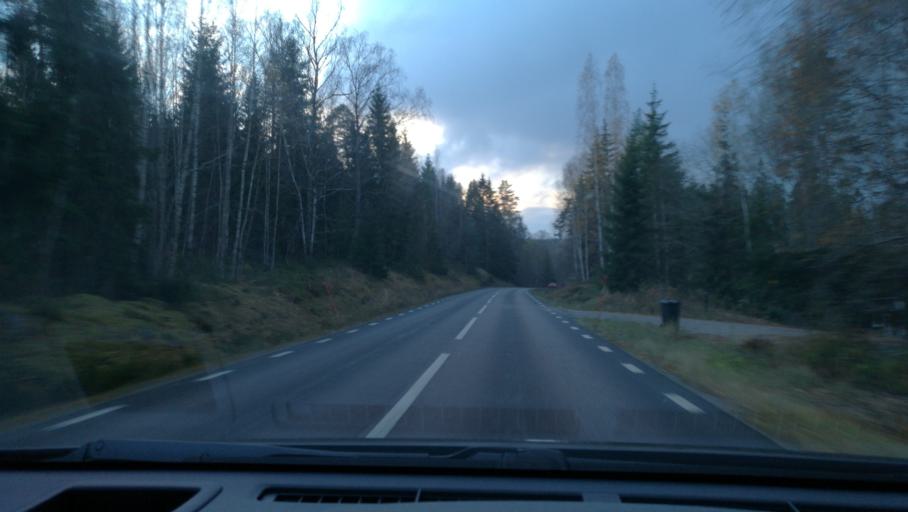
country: SE
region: Soedermanland
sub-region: Vingakers Kommun
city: Vingaker
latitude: 59.1350
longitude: 15.8436
